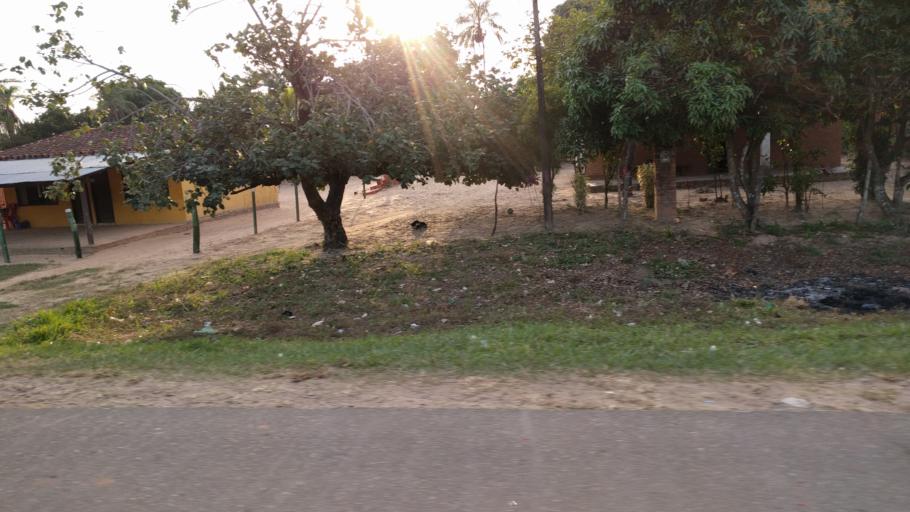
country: BO
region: Santa Cruz
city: Buena Vista
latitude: -17.4105
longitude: -63.6133
